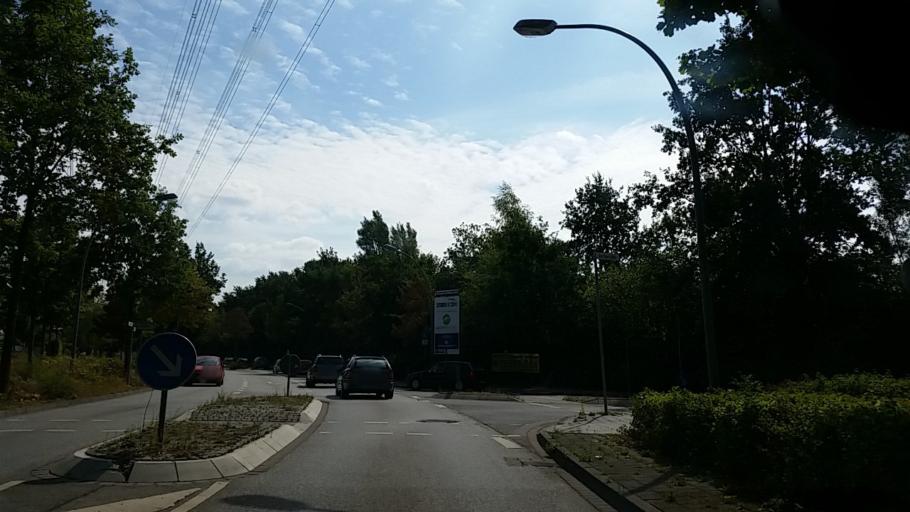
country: DE
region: Schleswig-Holstein
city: Wentorf bei Hamburg
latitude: 53.4880
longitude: 10.2531
